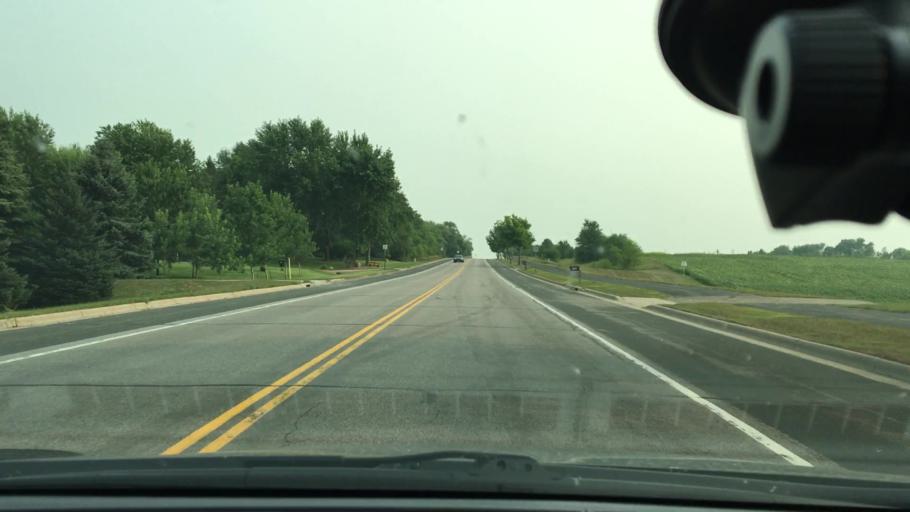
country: US
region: Minnesota
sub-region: Wright County
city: Otsego
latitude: 45.2574
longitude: -93.5913
